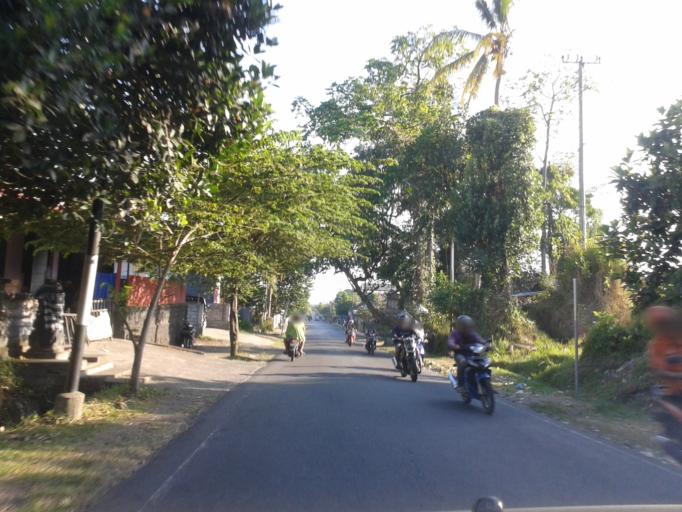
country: ID
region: Bali
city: Klungkung
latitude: -8.5105
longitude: 115.4021
